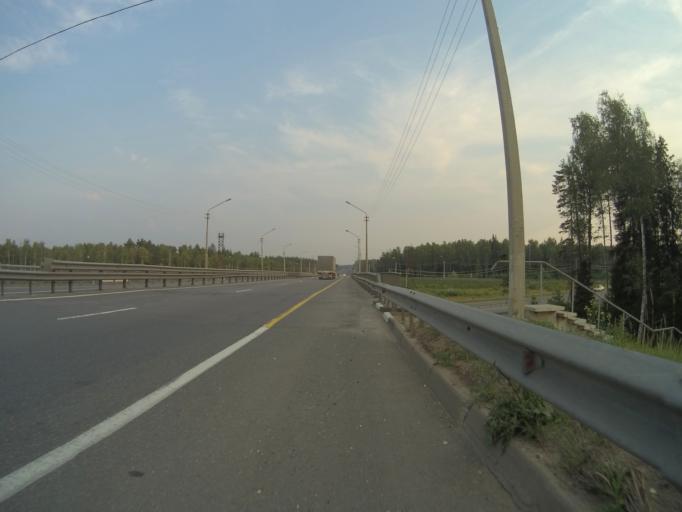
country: RU
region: Vladimir
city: Kameshkovo
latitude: 56.1950
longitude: 40.9518
